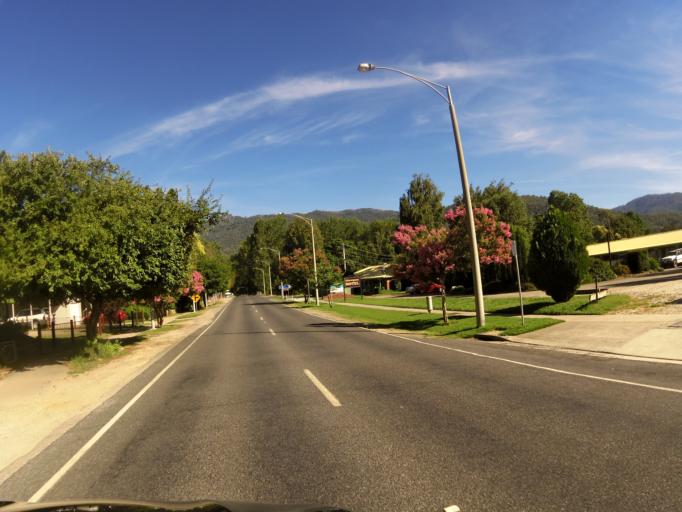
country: AU
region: Victoria
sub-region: Alpine
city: Mount Beauty
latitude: -36.7384
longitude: 147.1615
